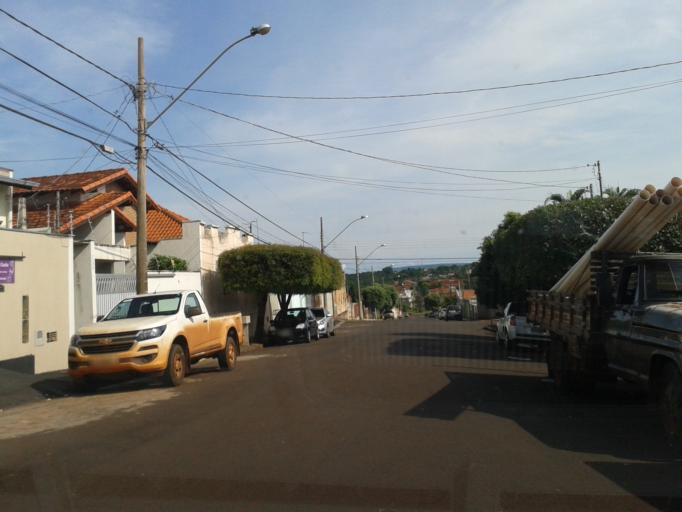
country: BR
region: Minas Gerais
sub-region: Ituiutaba
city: Ituiutaba
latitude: -18.9734
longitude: -49.4571
